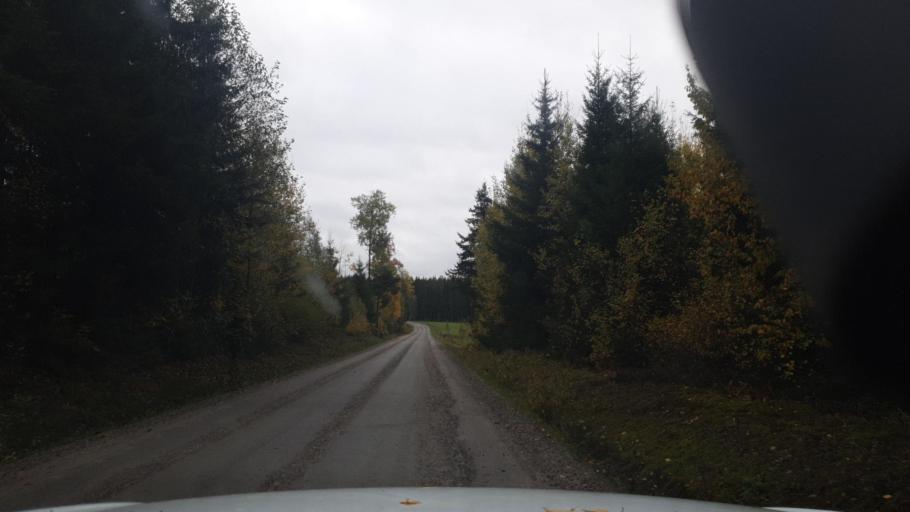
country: SE
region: Vaermland
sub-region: Karlstads Kommun
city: Edsvalla
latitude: 59.4916
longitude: 13.0312
